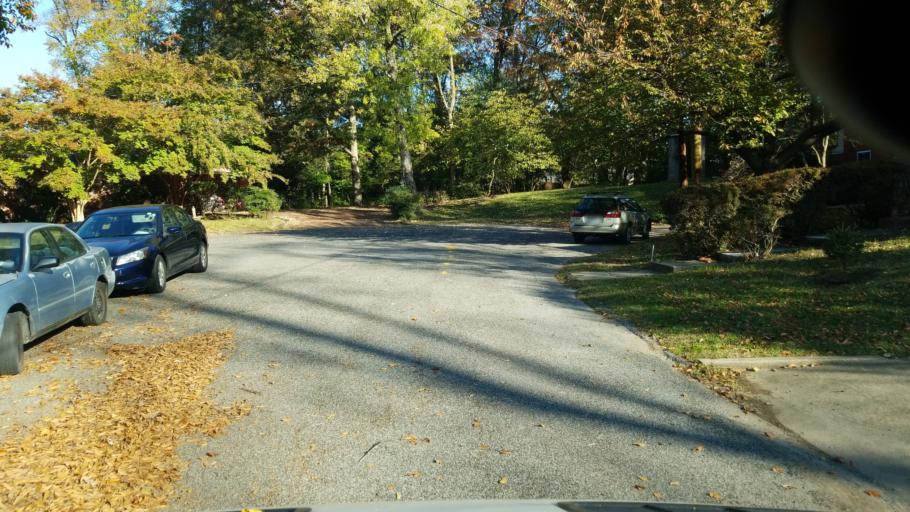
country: US
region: Maryland
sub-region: Montgomery County
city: Chevy Chase
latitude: 38.9732
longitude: -77.0554
